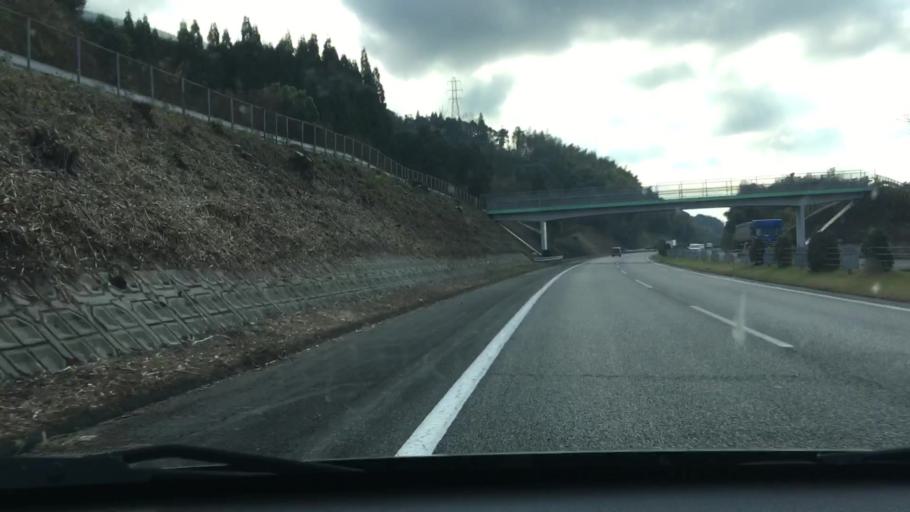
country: JP
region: Kumamoto
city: Yatsushiro
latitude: 32.5336
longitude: 130.6711
